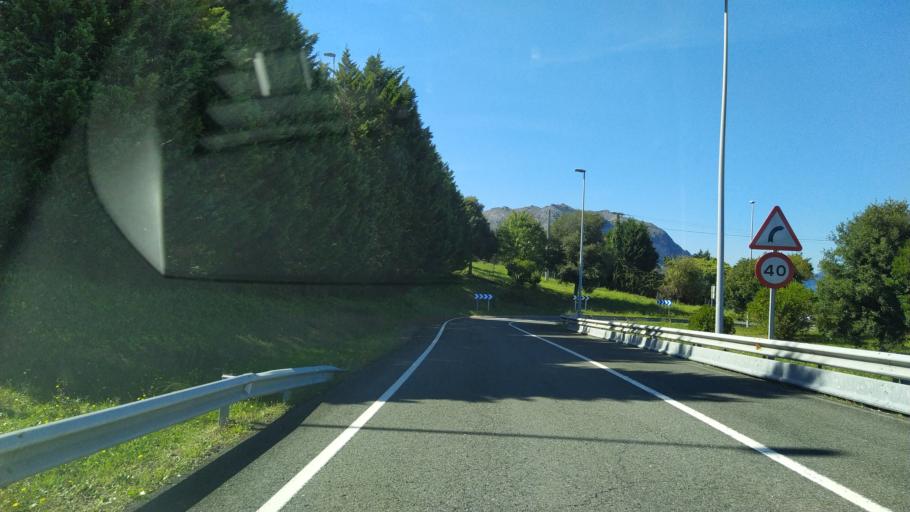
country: ES
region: Cantabria
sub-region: Provincia de Cantabria
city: Castro-Urdiales
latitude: 43.4026
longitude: -3.2916
